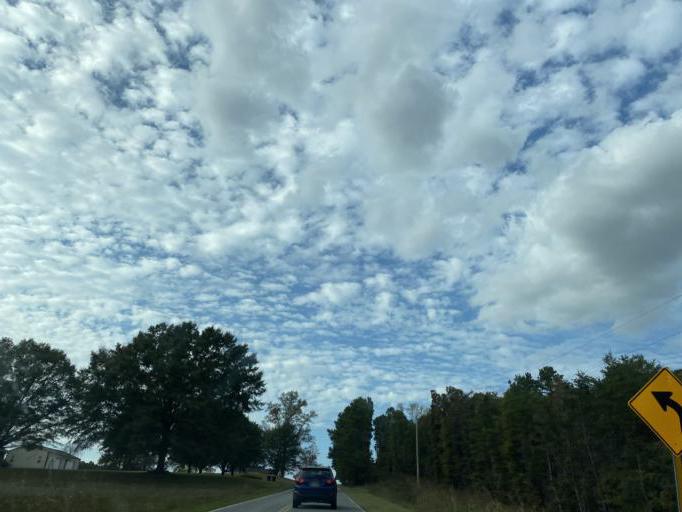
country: US
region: South Carolina
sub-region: Cherokee County
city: Gaffney
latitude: 35.0733
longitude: -81.7252
